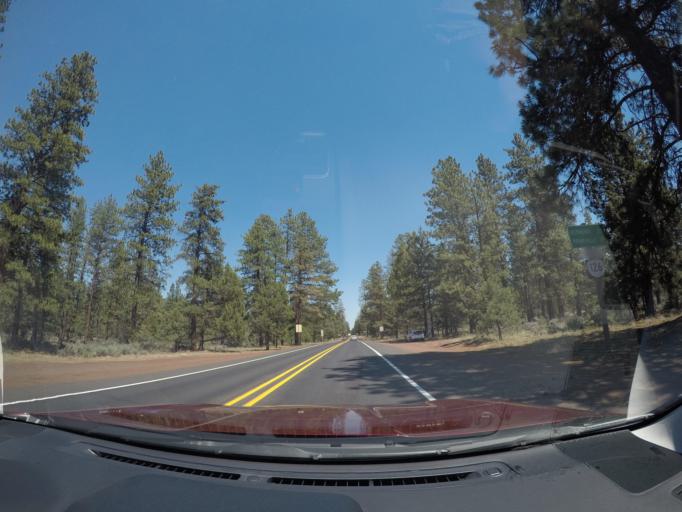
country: US
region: Oregon
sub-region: Deschutes County
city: Sisters
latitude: 44.2877
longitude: -121.5389
